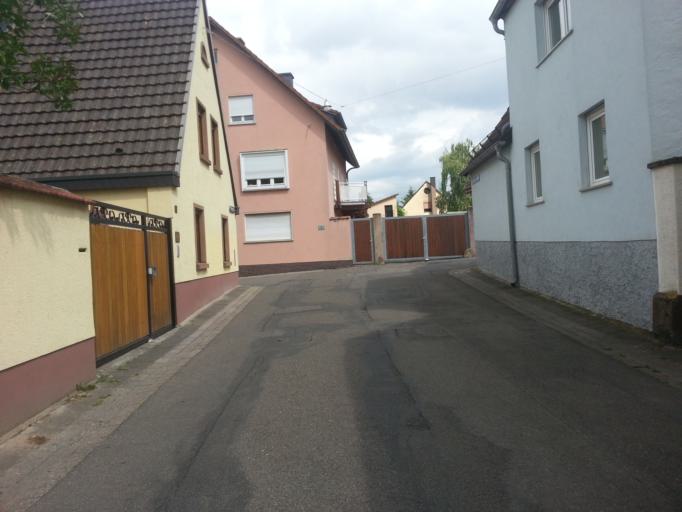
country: DE
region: Baden-Wuerttemberg
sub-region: Karlsruhe Region
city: Ilvesheim
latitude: 49.4885
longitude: 8.5363
